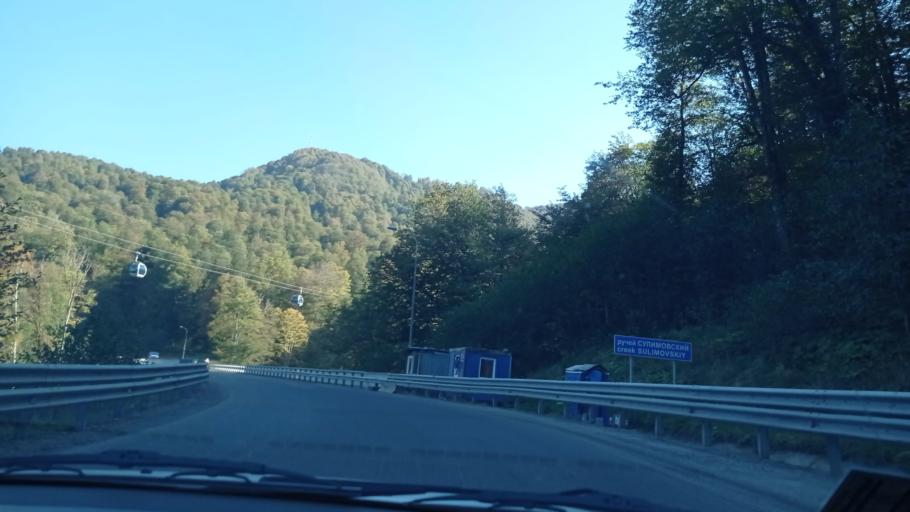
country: RU
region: Krasnodarskiy
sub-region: Sochi City
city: Krasnaya Polyana
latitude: 43.6596
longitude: 40.3002
